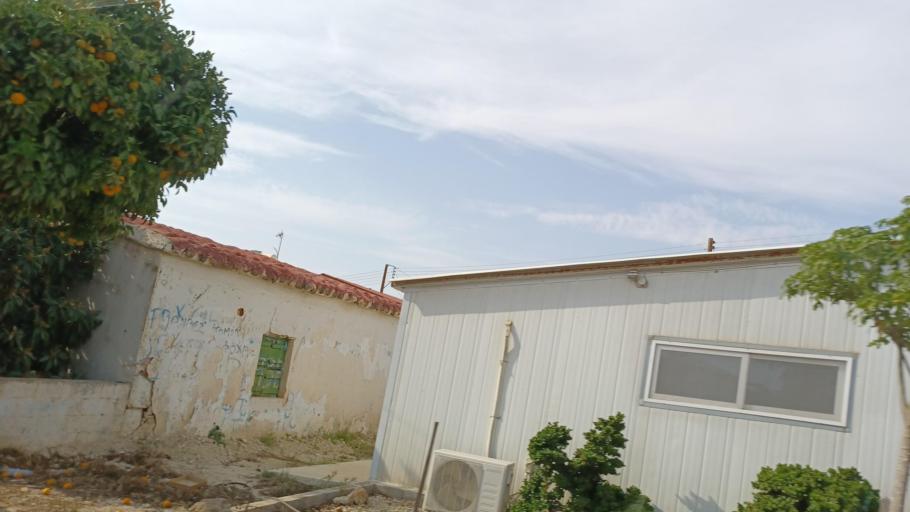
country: CY
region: Ammochostos
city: Frenaros
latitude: 35.0396
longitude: 33.9199
